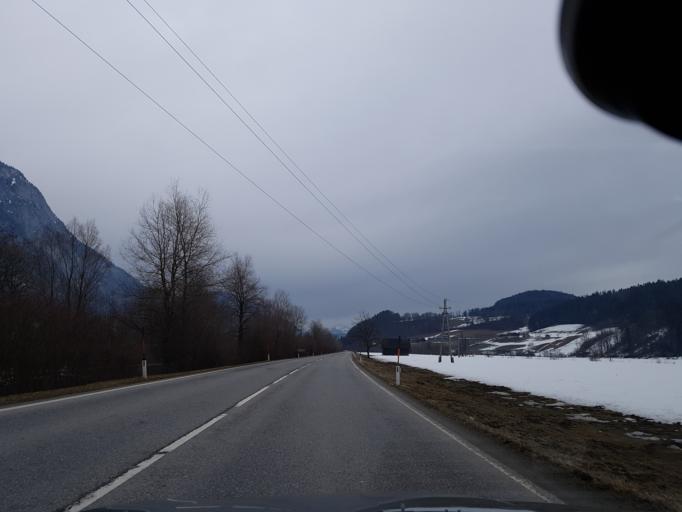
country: AT
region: Tyrol
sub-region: Politischer Bezirk Kufstein
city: Schwoich
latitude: 47.5400
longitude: 12.1161
